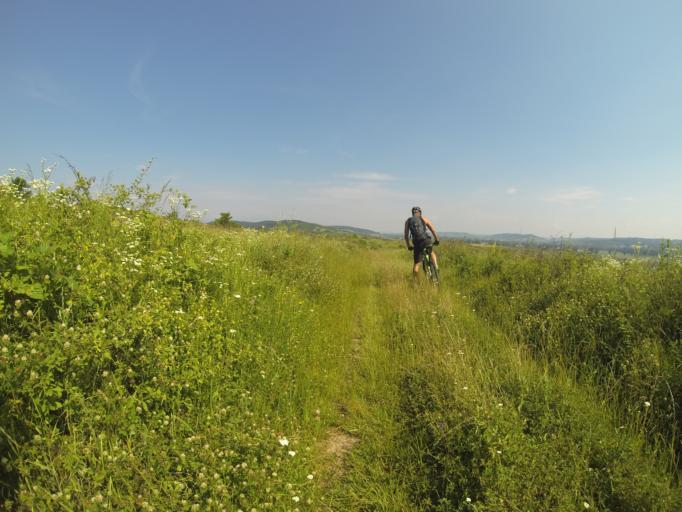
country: RO
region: Gorj
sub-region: Comuna Crusetu
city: Crusetu
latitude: 44.6094
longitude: 23.6694
